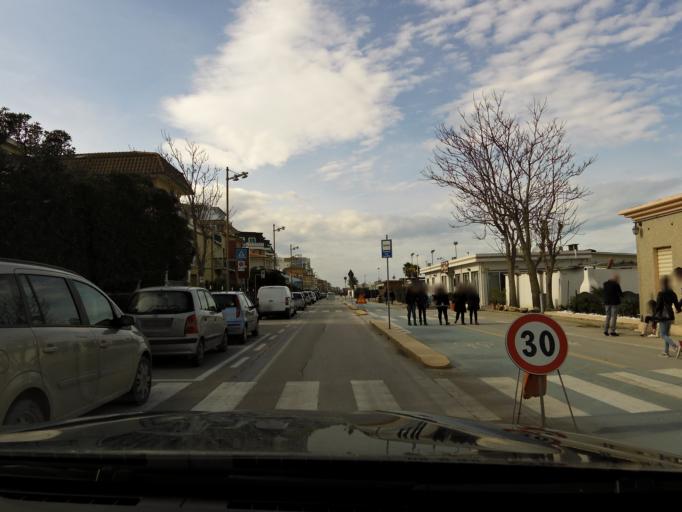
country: IT
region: The Marches
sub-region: Provincia di Macerata
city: Civitanova Marche
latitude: 43.3190
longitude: 13.7214
